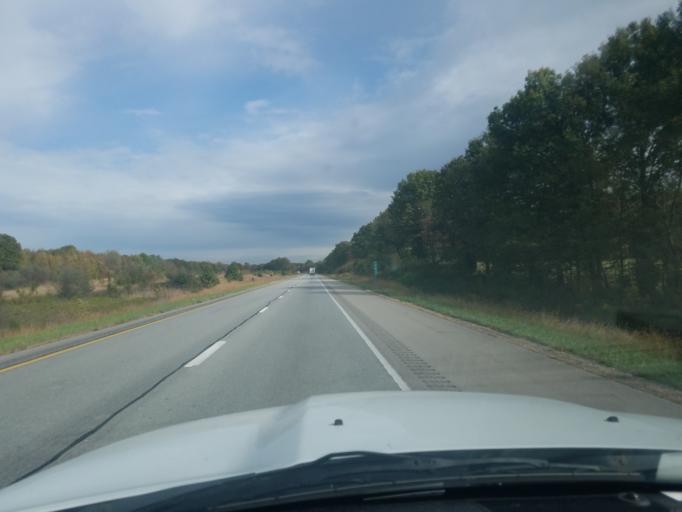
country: US
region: Indiana
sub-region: Warrick County
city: Chandler
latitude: 38.1833
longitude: -87.3811
